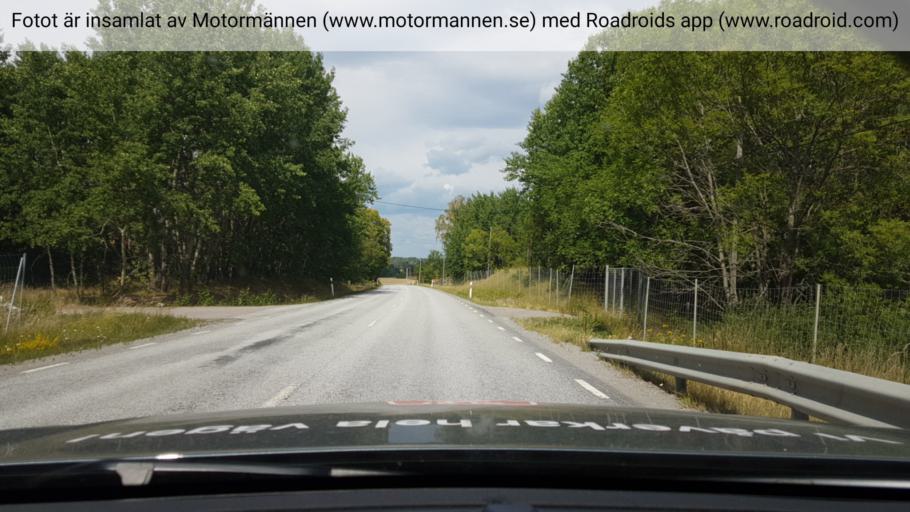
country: SE
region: Uppsala
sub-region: Habo Kommun
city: Balsta
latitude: 59.6116
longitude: 17.6060
